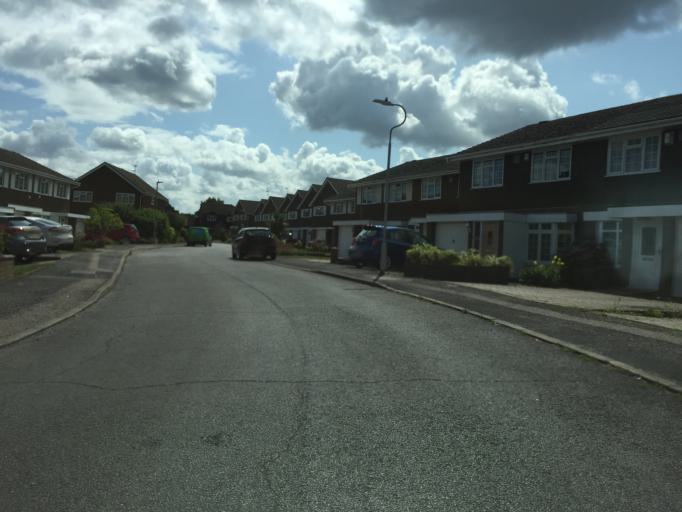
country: GB
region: England
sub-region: Kent
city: Larkfield
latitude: 51.2937
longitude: 0.4519
